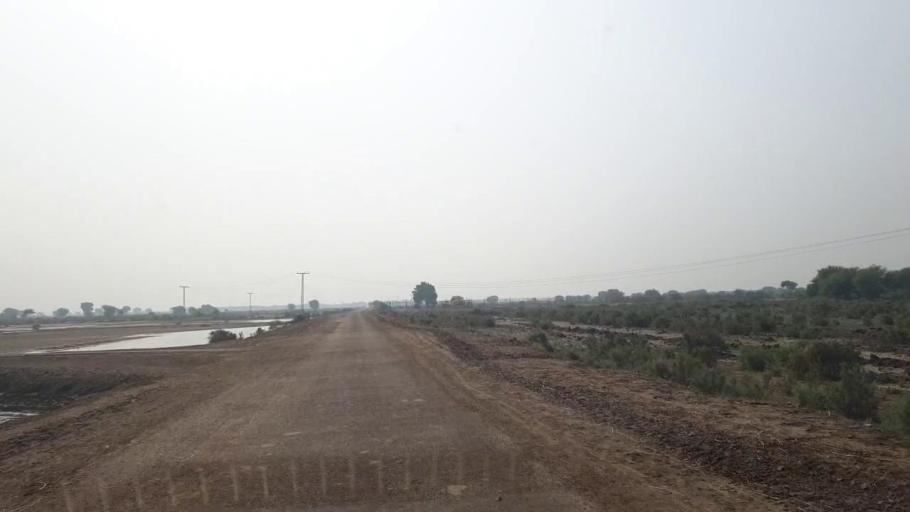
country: PK
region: Sindh
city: Matli
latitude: 25.1401
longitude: 68.6906
